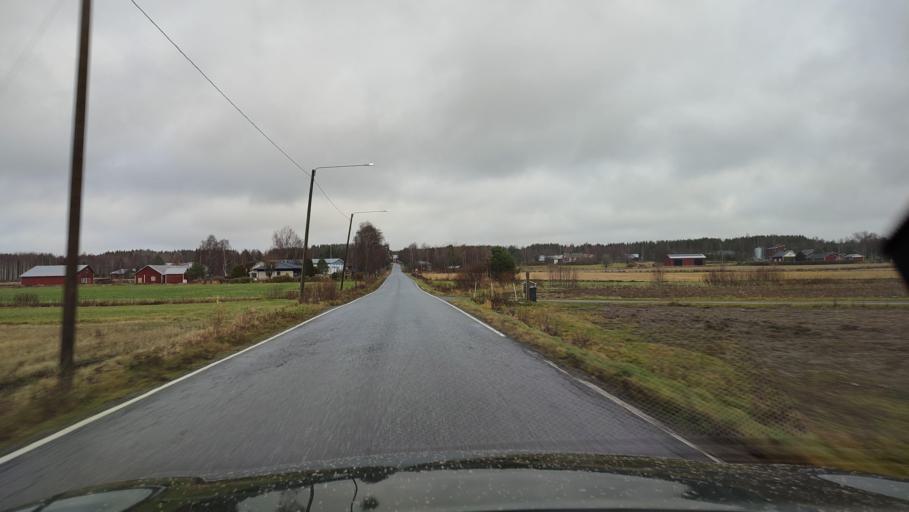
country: FI
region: Ostrobothnia
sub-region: Sydosterbotten
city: Kristinestad
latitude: 62.3102
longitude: 21.4812
